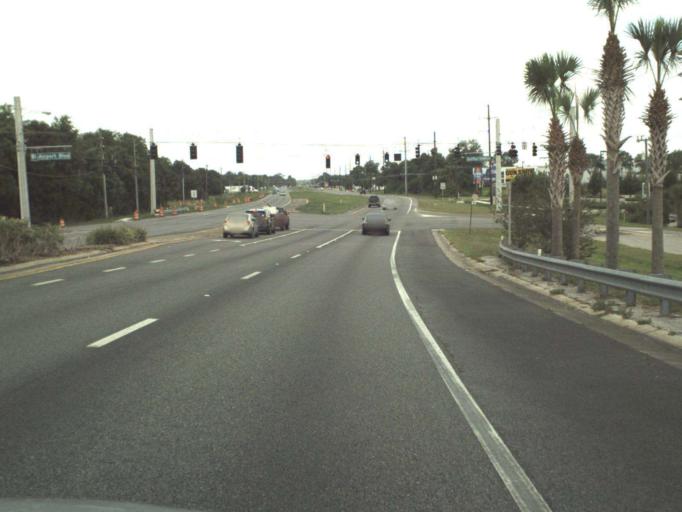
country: US
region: Florida
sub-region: Seminole County
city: Sanford
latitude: 28.8113
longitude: -81.2970
